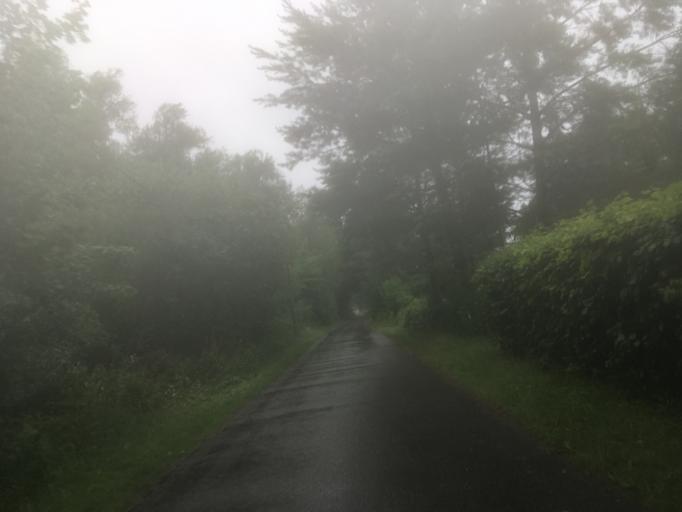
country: DE
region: Brandenburg
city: Zehdenick
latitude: 53.0005
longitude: 13.3191
